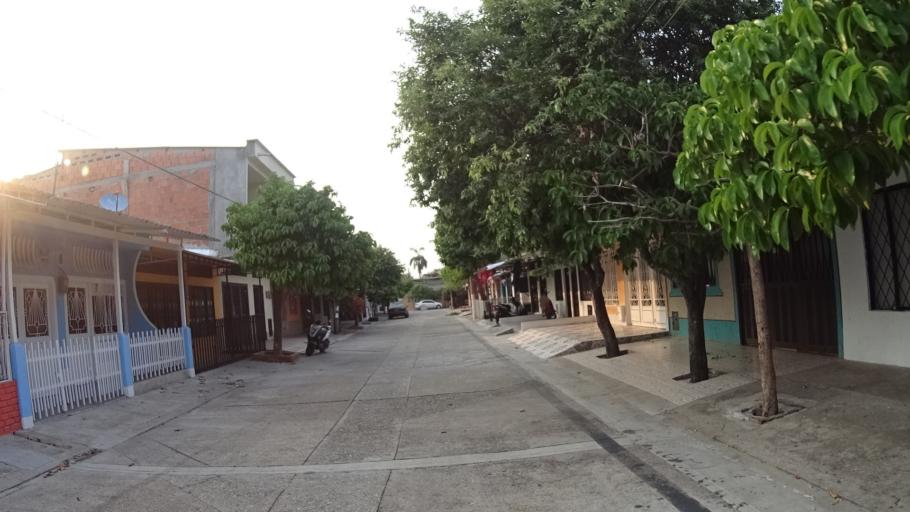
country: CO
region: Caldas
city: La Dorada
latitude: 5.4448
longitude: -74.6585
